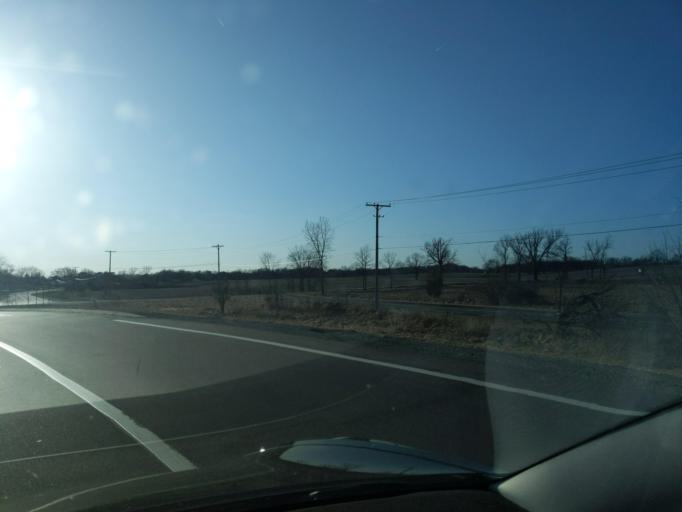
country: US
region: Michigan
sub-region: Washtenaw County
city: Chelsea
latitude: 42.2994
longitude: -83.9749
